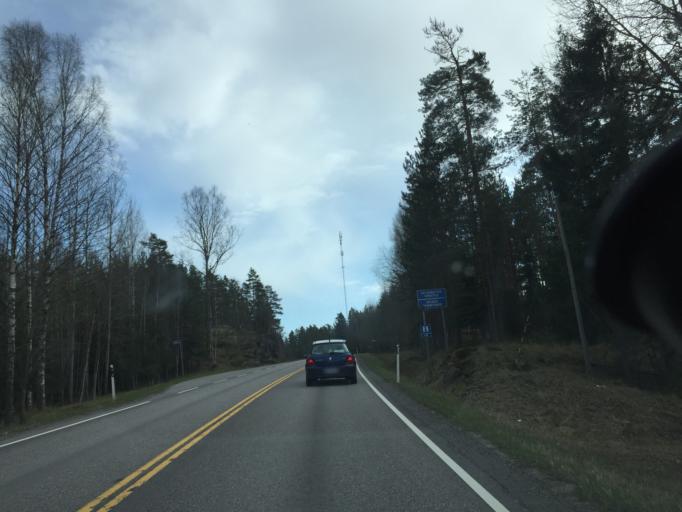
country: FI
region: Uusimaa
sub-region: Raaseporin
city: Ekenaes
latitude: 60.0222
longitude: 23.3764
